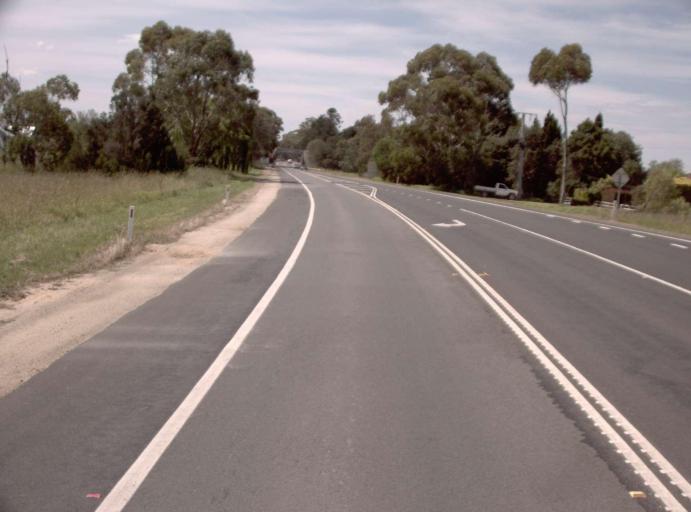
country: AU
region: Victoria
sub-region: Wellington
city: Sale
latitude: -37.9815
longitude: 147.0721
